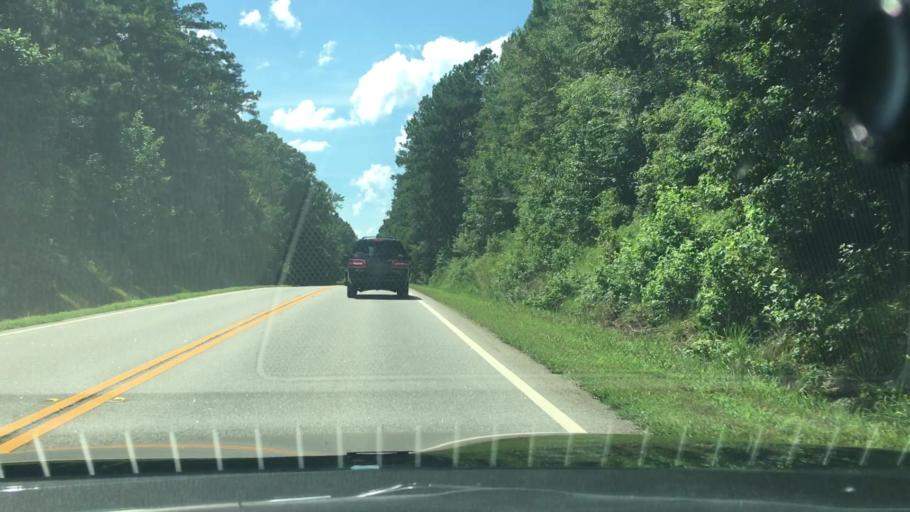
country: US
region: Georgia
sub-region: Putnam County
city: Eatonton
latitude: 33.3104
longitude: -83.5220
